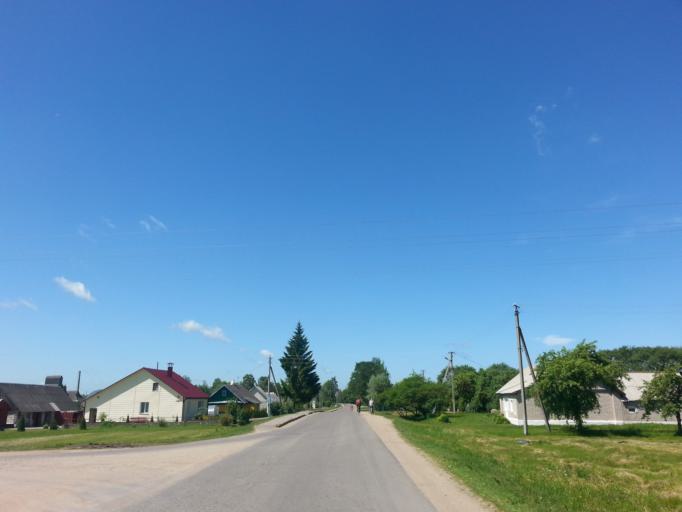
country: BY
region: Vitebsk
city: Mosar
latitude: 55.2108
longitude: 27.5698
